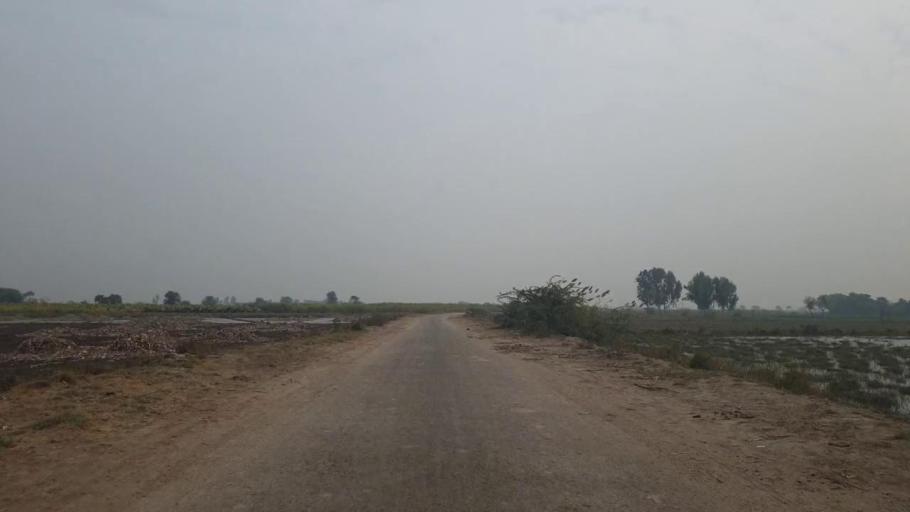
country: PK
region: Sindh
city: Tando Adam
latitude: 25.7234
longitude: 68.7120
